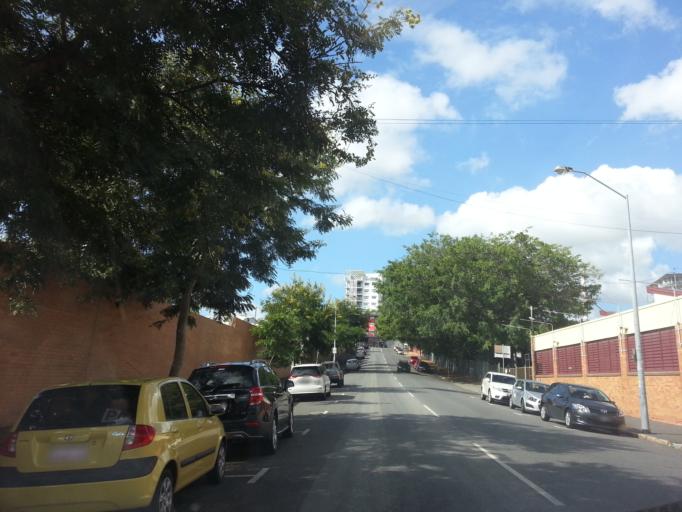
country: AU
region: Queensland
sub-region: Brisbane
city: Fortitude Valley
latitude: -27.4507
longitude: 153.0333
